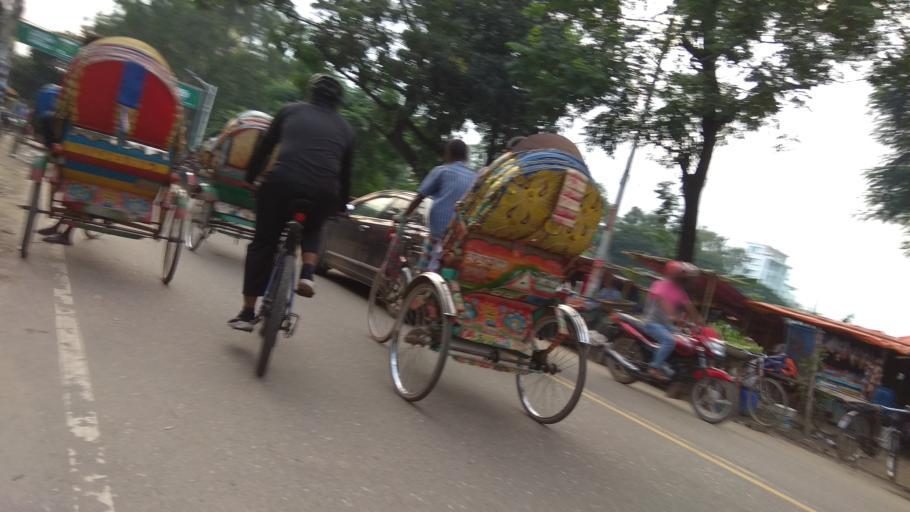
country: BD
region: Dhaka
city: Tungi
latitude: 23.8645
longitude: 90.3933
